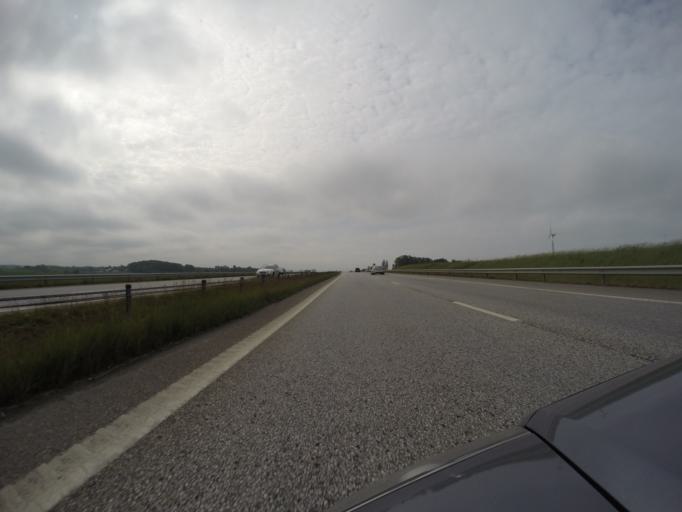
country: SE
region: Skane
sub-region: Landskrona
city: Landskrona
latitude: 55.8668
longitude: 12.8799
